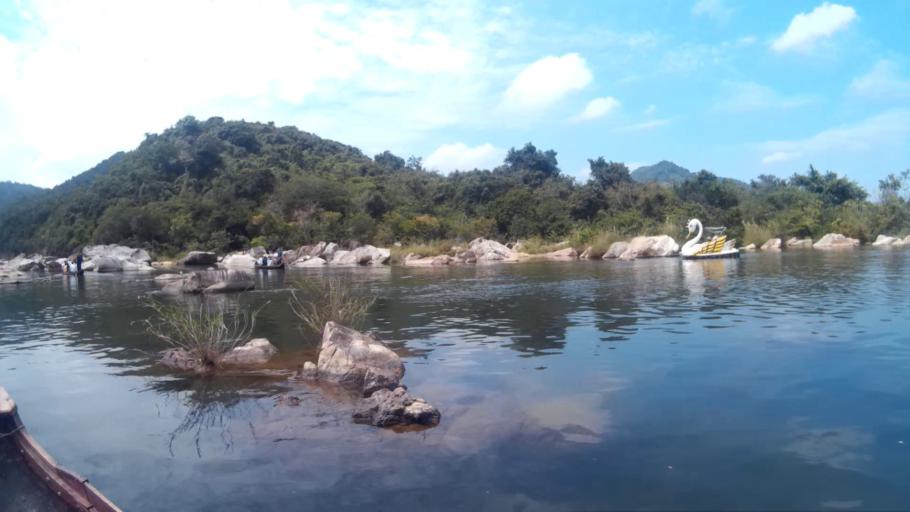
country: VN
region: Binh Dinh
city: Phu Phong
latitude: 13.8732
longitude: 108.8618
